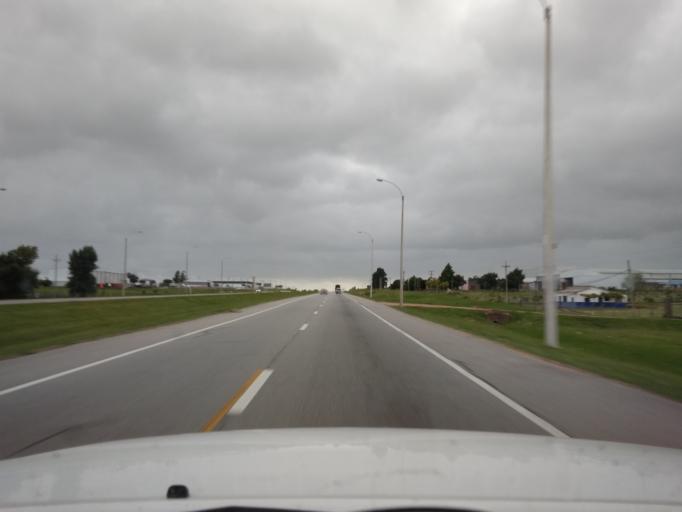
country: UY
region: Canelones
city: Las Piedras
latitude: -34.6979
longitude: -56.2389
